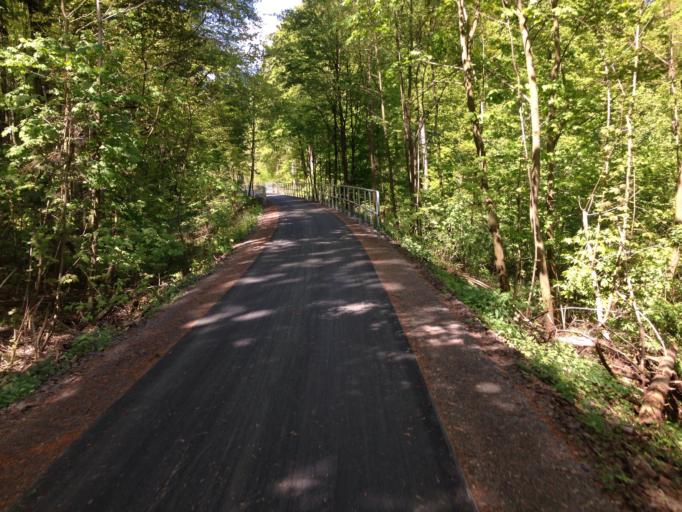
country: DE
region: Hesse
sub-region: Regierungsbezirk Giessen
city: Laubach
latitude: 50.5316
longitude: 8.9497
